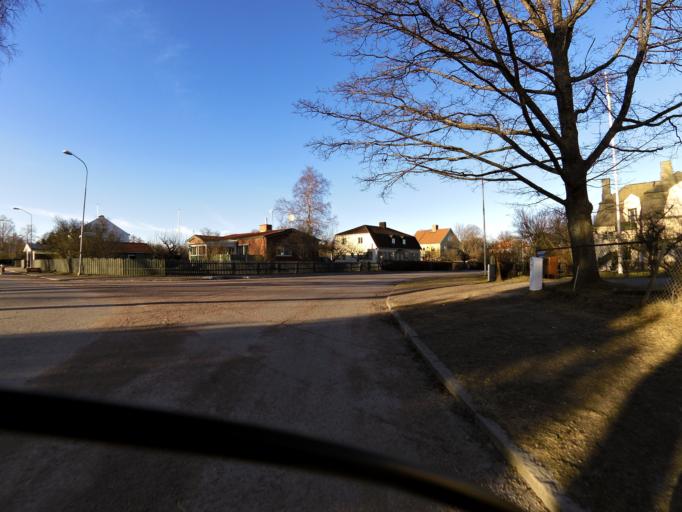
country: SE
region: Gaevleborg
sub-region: Gavle Kommun
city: Gavle
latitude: 60.6697
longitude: 17.1245
